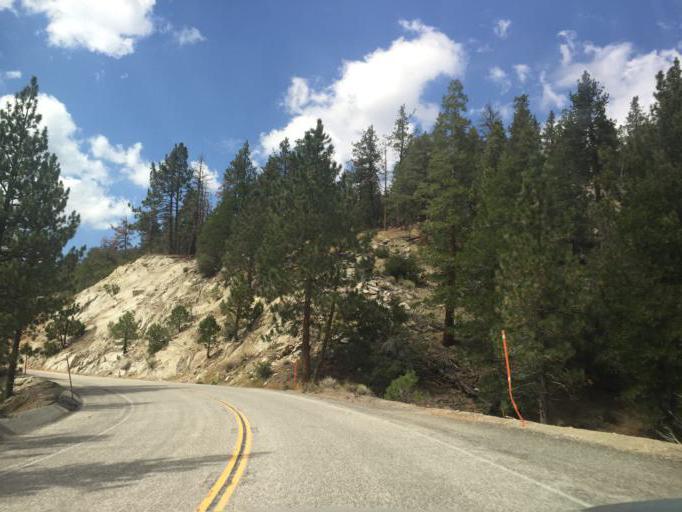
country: US
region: California
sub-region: Los Angeles County
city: Littlerock
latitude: 34.3505
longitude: -117.9408
